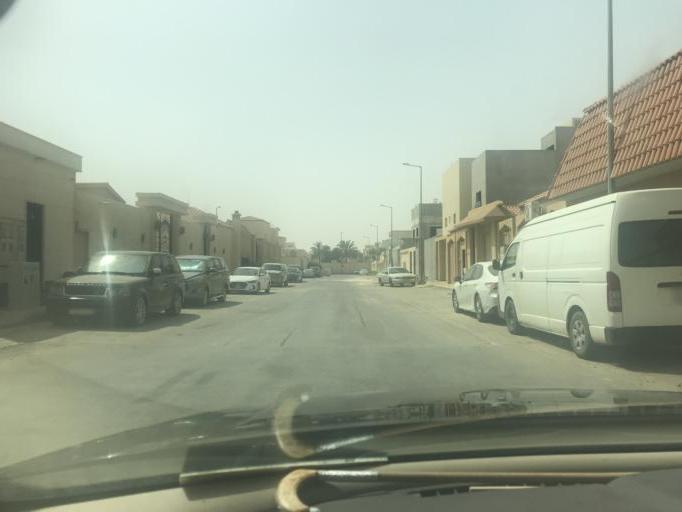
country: SA
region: Ar Riyad
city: Riyadh
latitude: 24.7425
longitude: 46.7865
